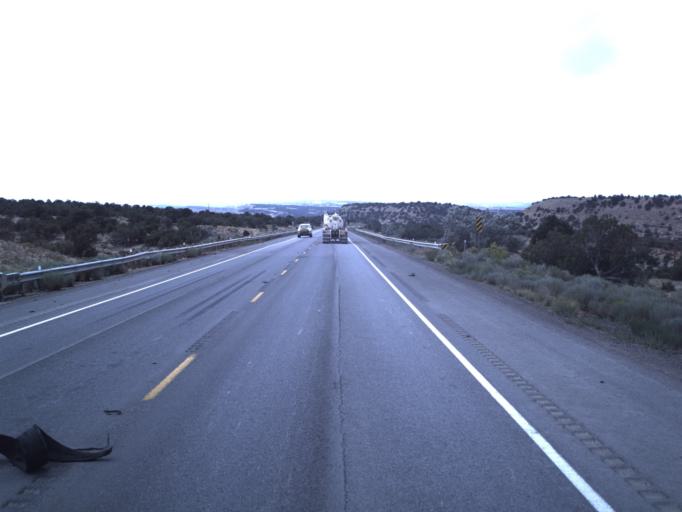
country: US
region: Utah
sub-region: Duchesne County
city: Duchesne
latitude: 40.1653
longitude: -110.4725
